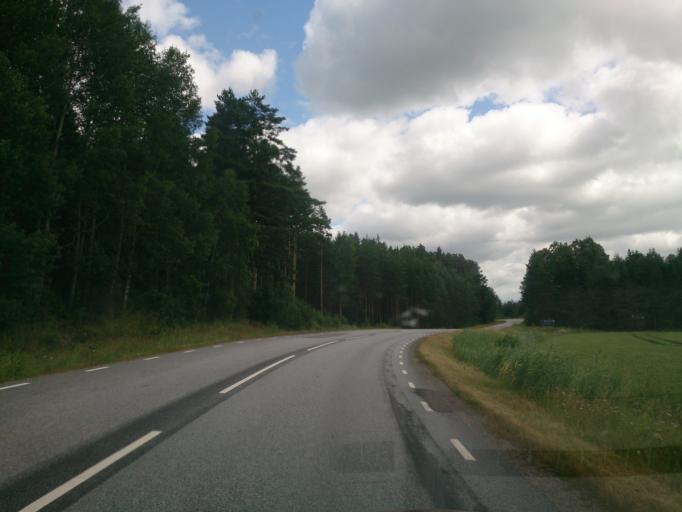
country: SE
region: OEstergoetland
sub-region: Soderkopings Kommun
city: Soederkoeping
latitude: 58.5096
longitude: 16.3292
